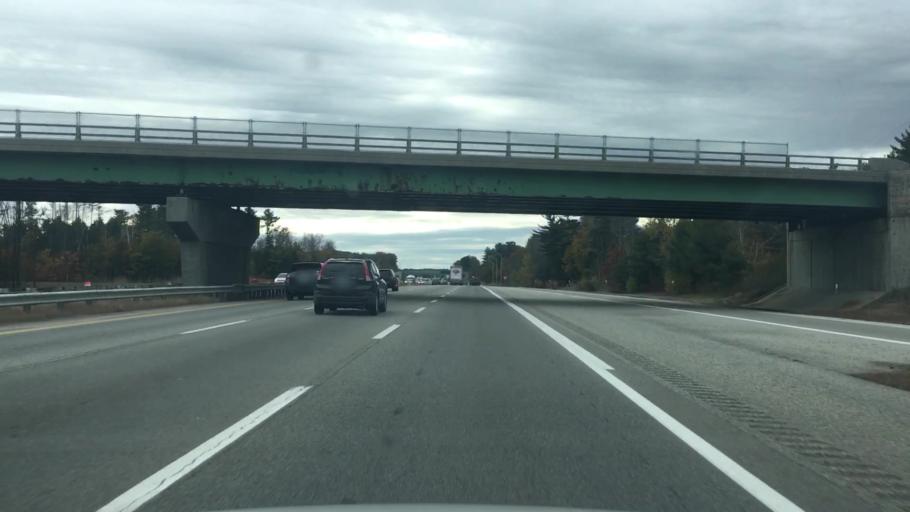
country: US
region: Maine
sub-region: Cumberland County
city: West Scarborough
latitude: 43.6054
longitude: -70.3723
